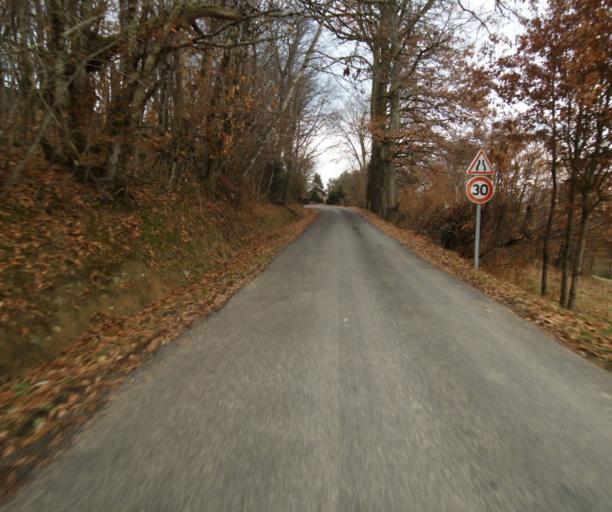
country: FR
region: Limousin
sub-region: Departement de la Correze
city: Chameyrat
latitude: 45.2394
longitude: 1.7249
